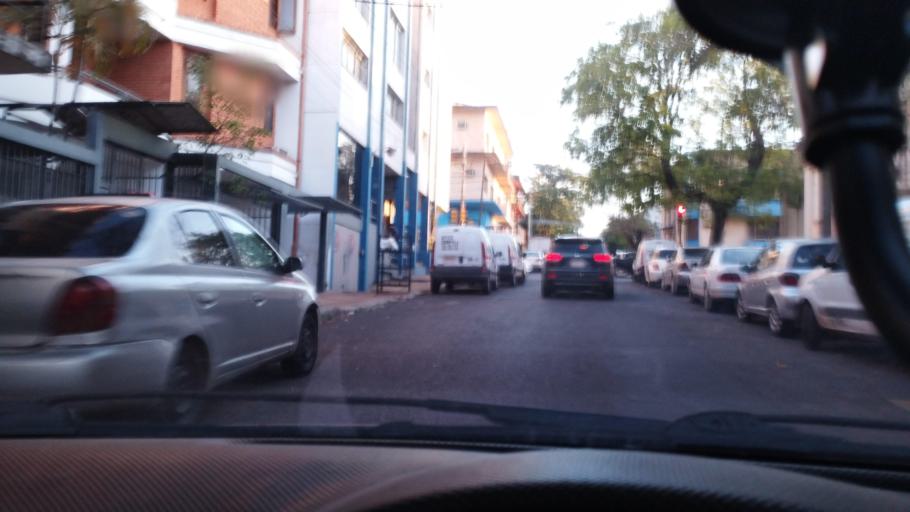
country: PY
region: Asuncion
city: Asuncion
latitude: -25.2956
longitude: -57.6148
